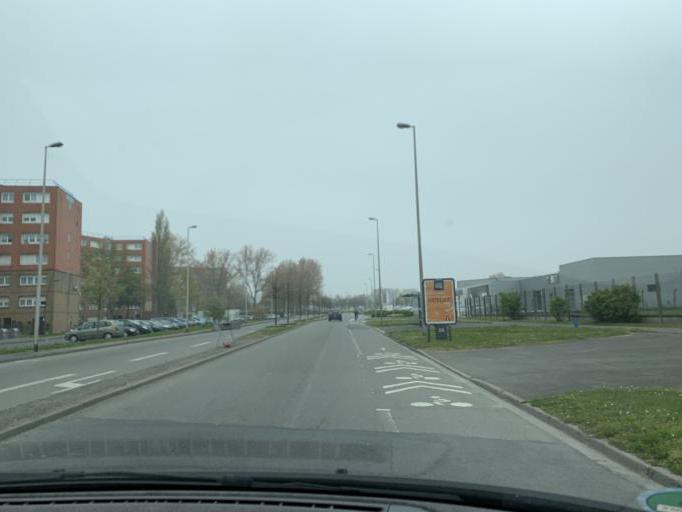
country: FR
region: Nord-Pas-de-Calais
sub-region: Departement du Nord
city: Dunkerque
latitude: 51.0223
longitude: 2.3599
